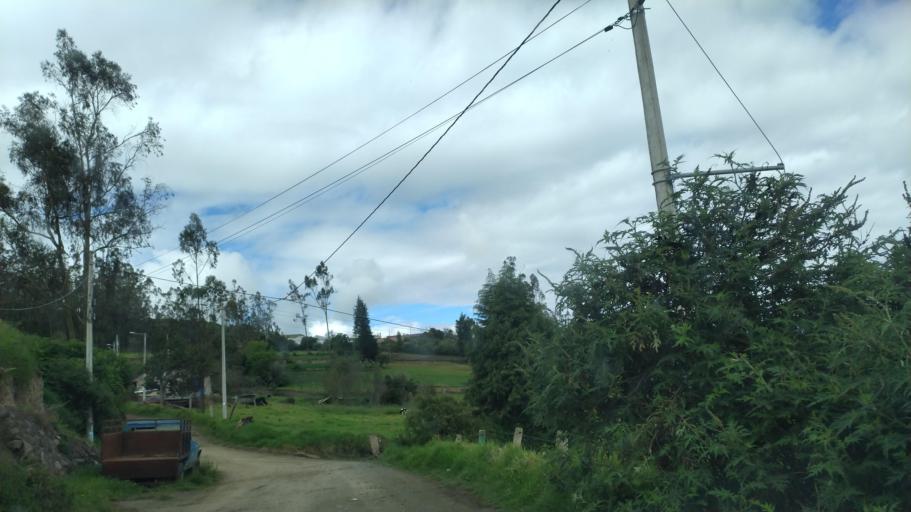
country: EC
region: Chimborazo
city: Riobamba
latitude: -1.6618
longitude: -78.5710
